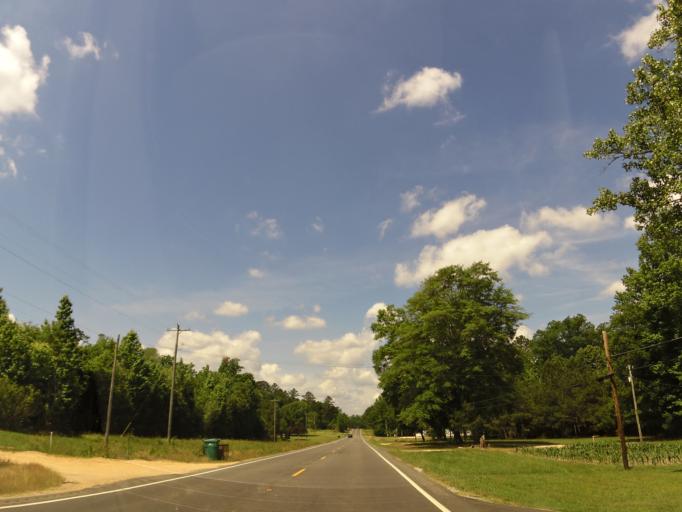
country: US
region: Alabama
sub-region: Lamar County
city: Sulligent
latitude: 33.9236
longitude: -88.0341
